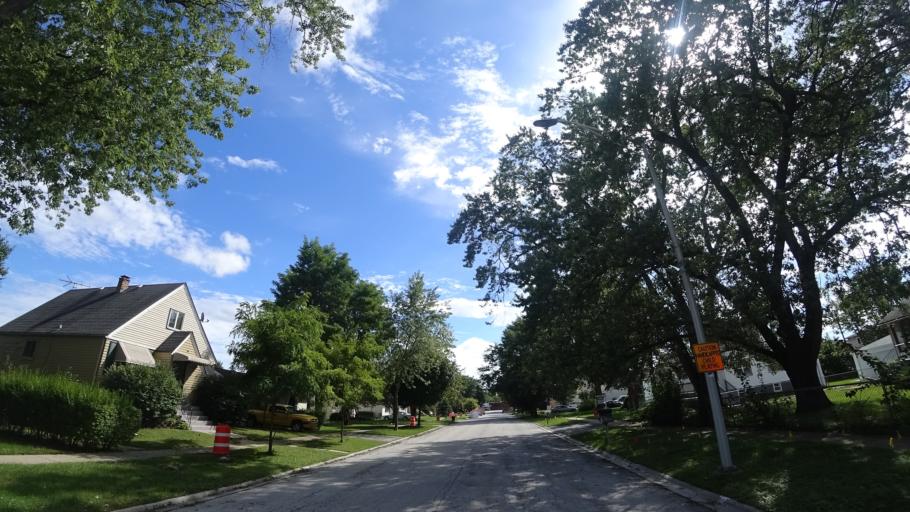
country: US
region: Illinois
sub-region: Cook County
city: Chicago Ridge
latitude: 41.7104
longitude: -87.7759
